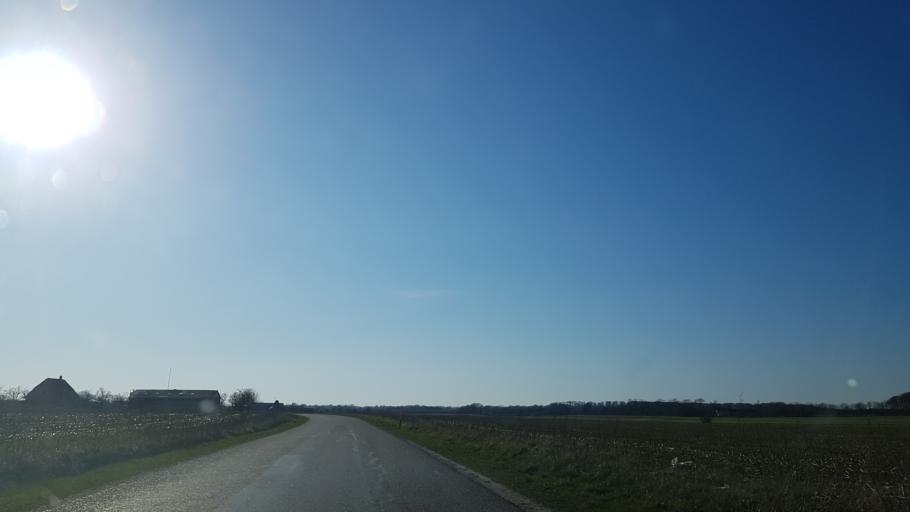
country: DK
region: South Denmark
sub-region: Vejen Kommune
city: Rodding
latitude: 55.3956
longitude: 9.0860
